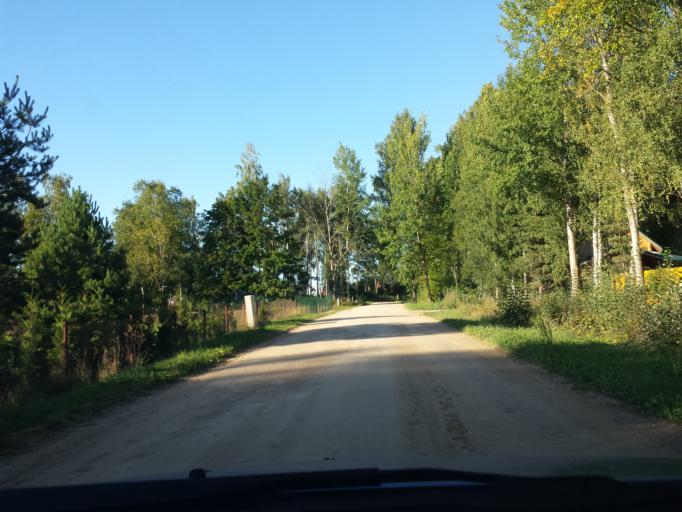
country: LV
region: Carnikava
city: Carnikava
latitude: 57.1168
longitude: 24.2345
